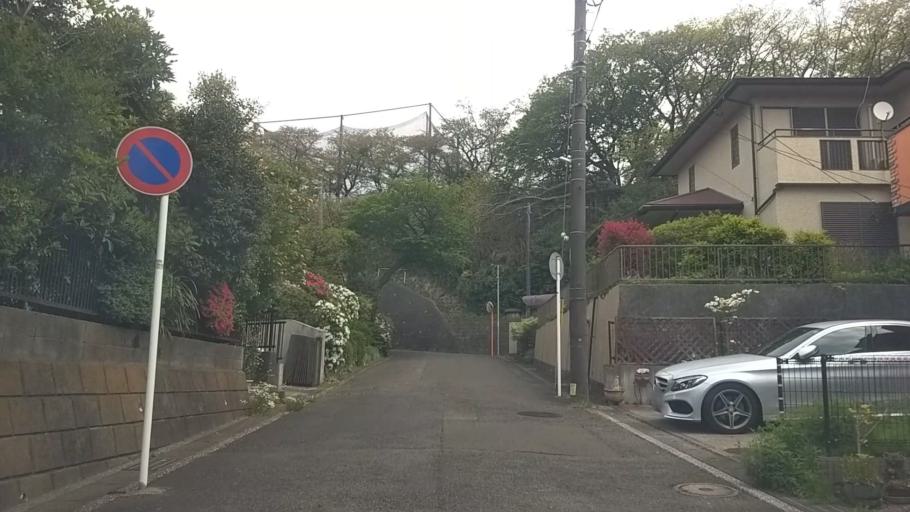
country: JP
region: Kanagawa
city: Kamakura
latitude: 35.3728
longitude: 139.6019
